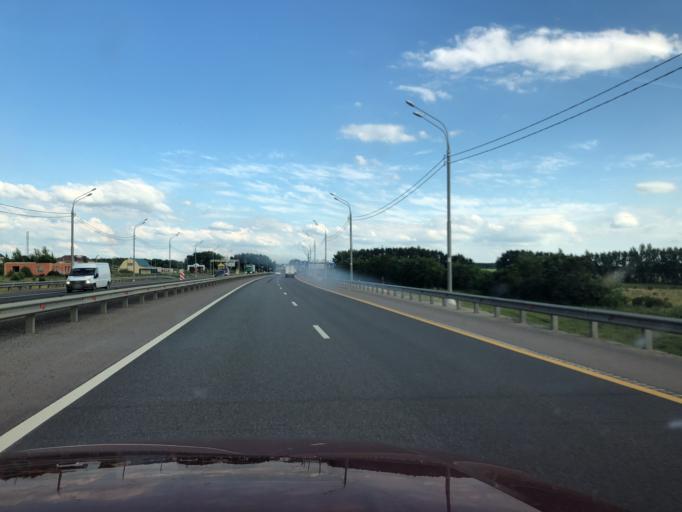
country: RU
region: Lipetsk
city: Zadonsk
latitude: 52.4354
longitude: 38.8171
